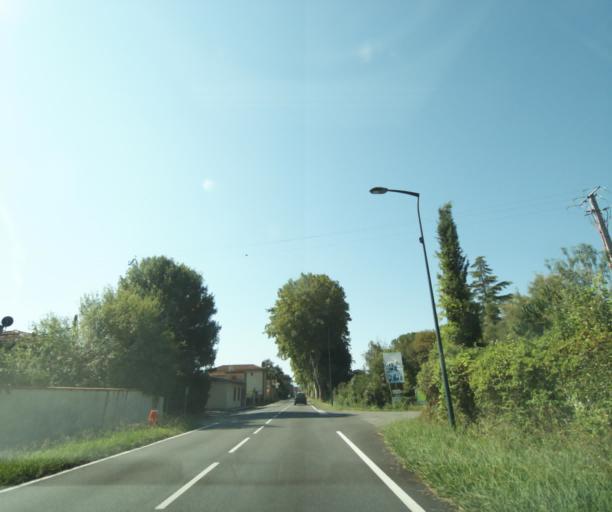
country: FR
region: Midi-Pyrenees
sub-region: Departement de la Haute-Garonne
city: Saint-Sulpice-sur-Leze
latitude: 43.3333
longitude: 1.3220
